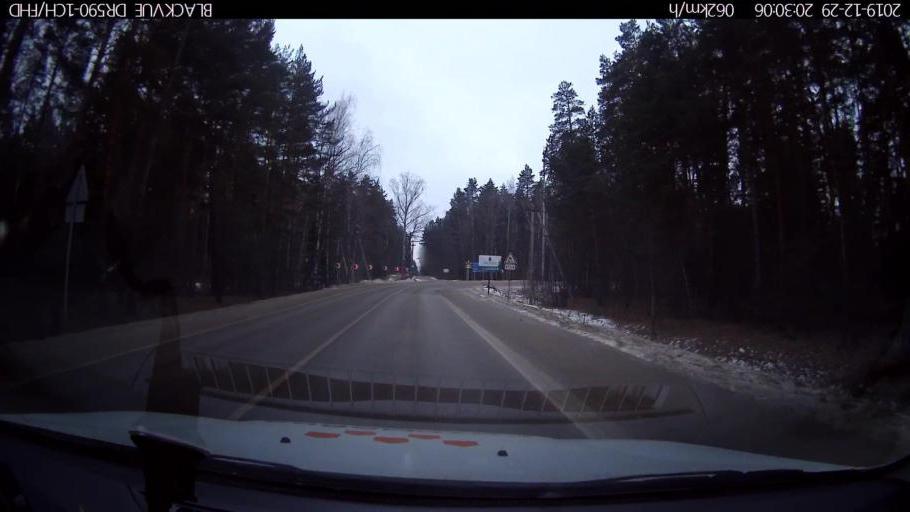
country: RU
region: Nizjnij Novgorod
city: Afonino
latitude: 56.1754
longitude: 44.0980
